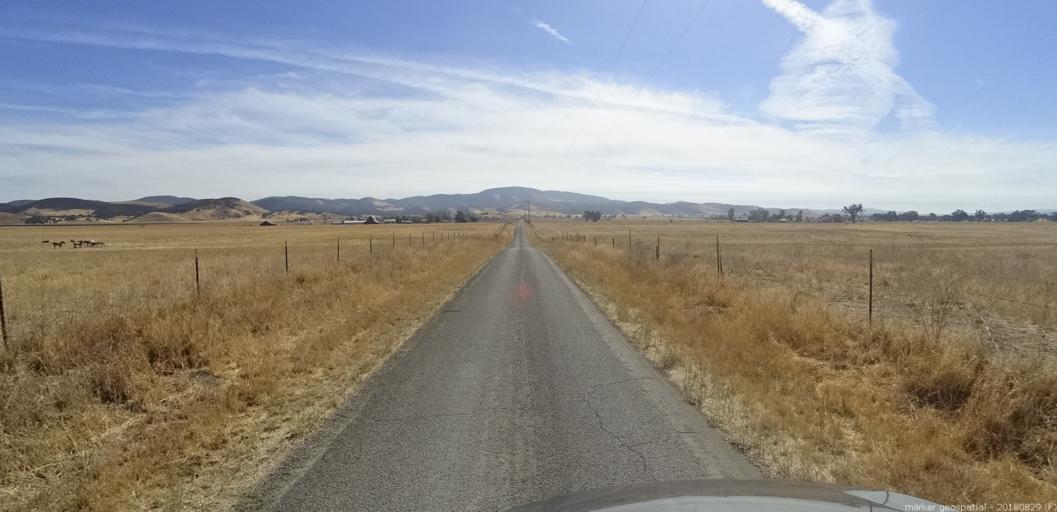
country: US
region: California
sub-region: Monterey County
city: King City
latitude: 35.9514
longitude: -121.0963
